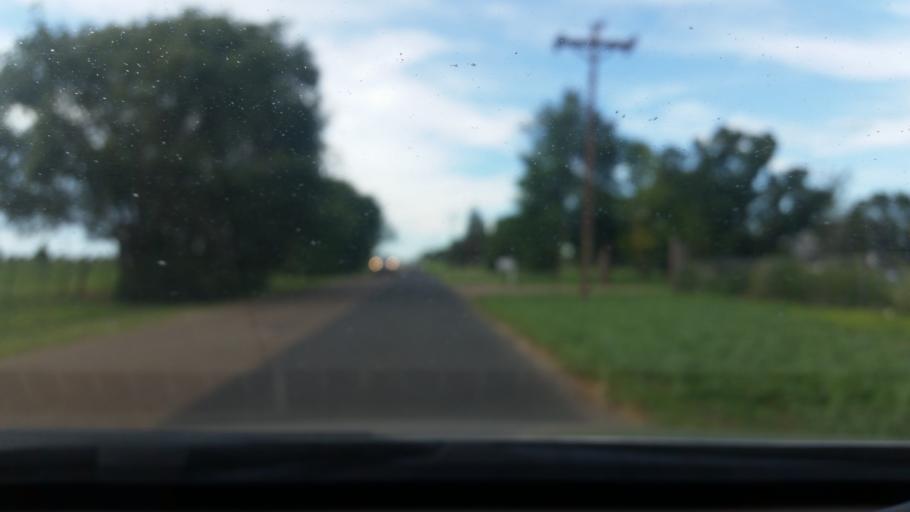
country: US
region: New Mexico
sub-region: Curry County
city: Clovis
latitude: 34.4515
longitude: -103.1784
